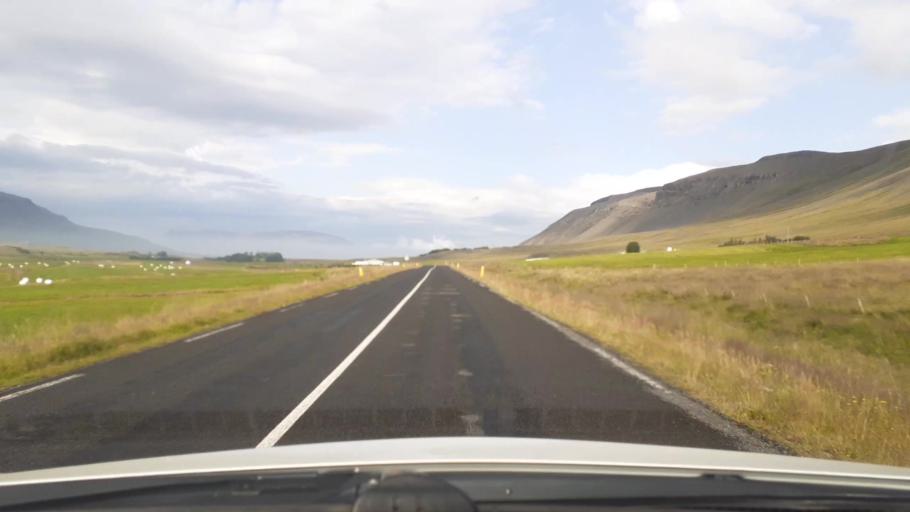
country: IS
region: Capital Region
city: Mosfellsbaer
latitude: 64.3422
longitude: -21.5591
